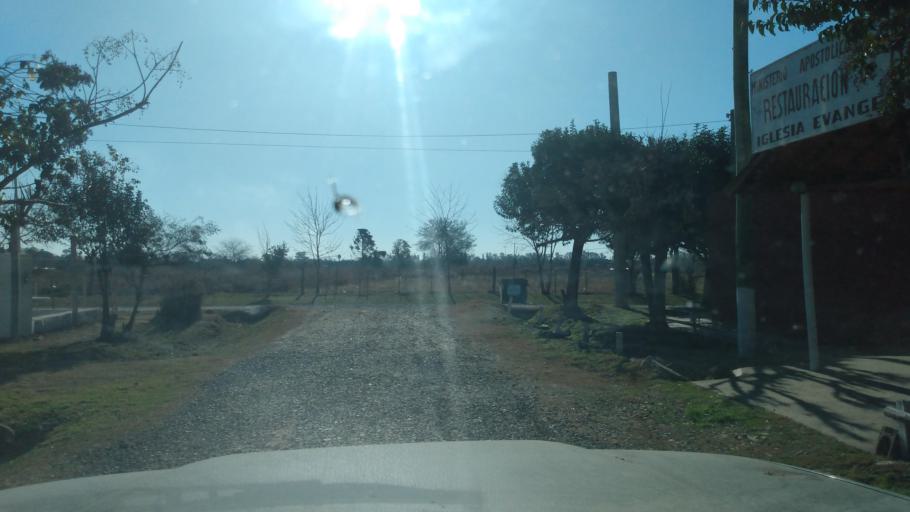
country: AR
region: Buenos Aires
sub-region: Partido de Lujan
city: Lujan
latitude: -34.5655
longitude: -59.0841
